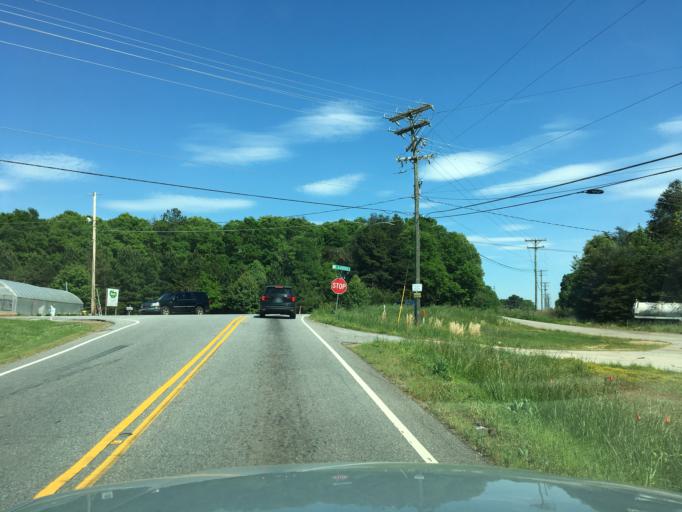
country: US
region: South Carolina
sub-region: Spartanburg County
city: Fairforest
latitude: 34.9695
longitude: -82.0332
